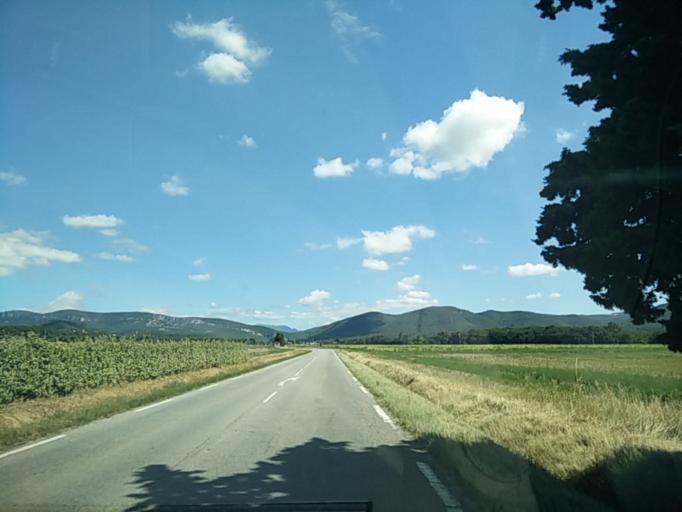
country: FR
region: Rhone-Alpes
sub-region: Departement de la Drome
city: La Begude-de-Mazenc
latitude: 44.5515
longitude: 4.9025
